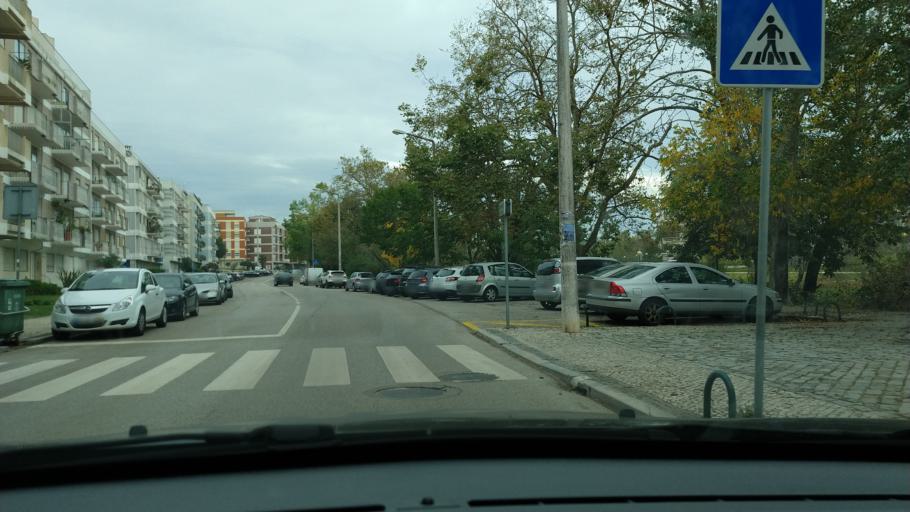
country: PT
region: Coimbra
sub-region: Figueira da Foz
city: Figueira da Foz
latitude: 40.1509
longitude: -8.8619
